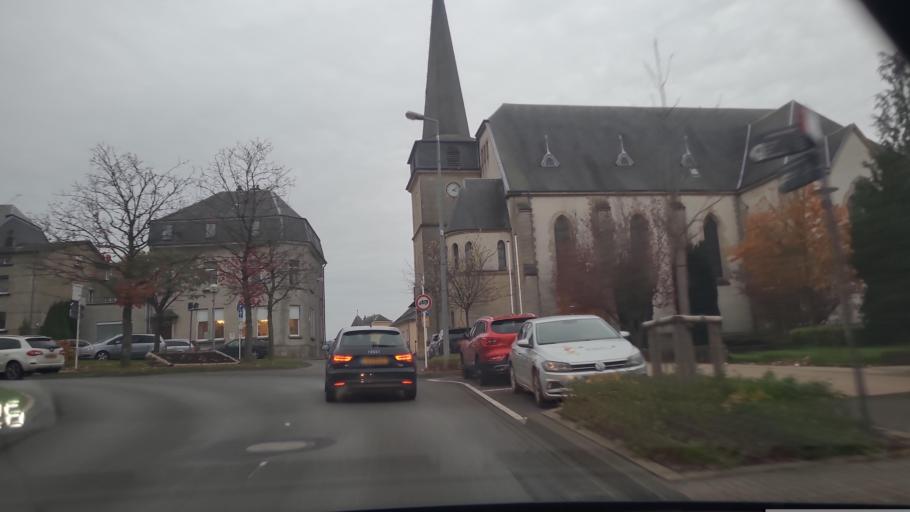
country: LU
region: Luxembourg
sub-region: Canton d'Esch-sur-Alzette
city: Obercorn
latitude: 49.5152
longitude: 5.8943
